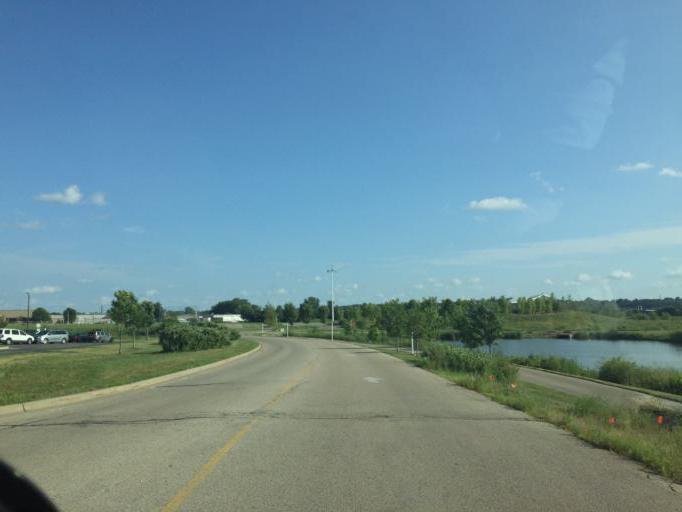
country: US
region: Minnesota
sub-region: Olmsted County
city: Rochester
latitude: 44.0423
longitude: -92.5056
